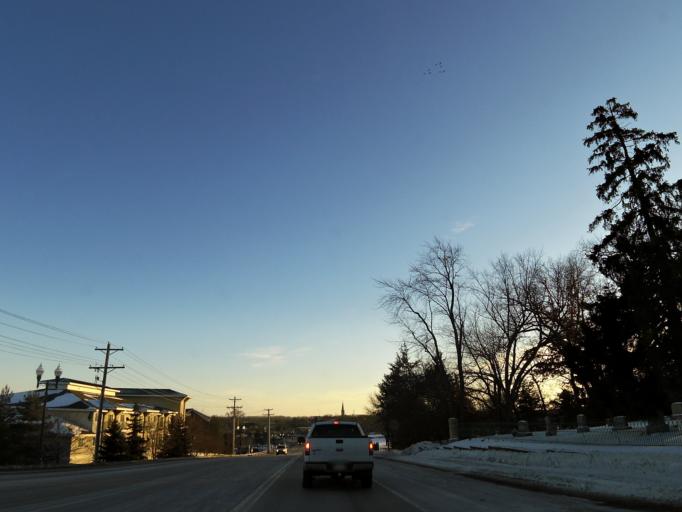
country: US
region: Minnesota
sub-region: Carver County
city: Chaska
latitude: 44.7931
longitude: -93.6022
